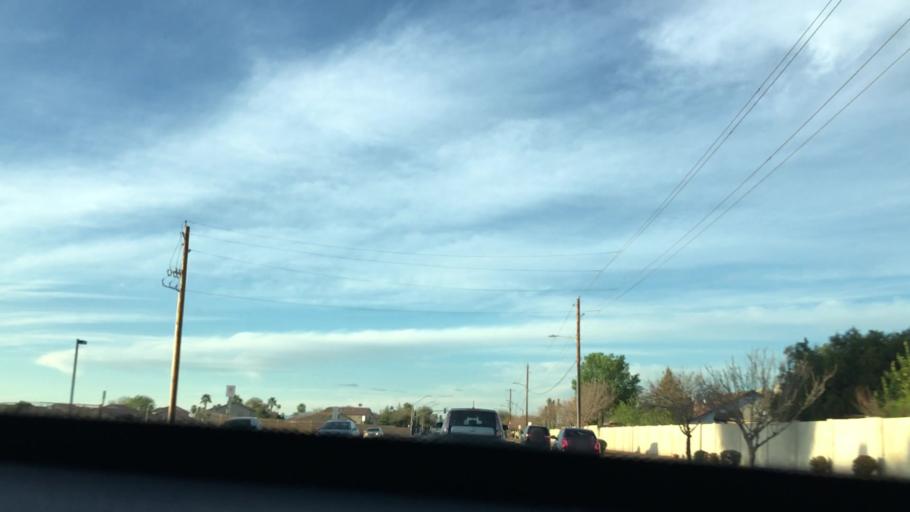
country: US
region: Arizona
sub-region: Maricopa County
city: Glendale
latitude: 33.5322
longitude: -112.2205
